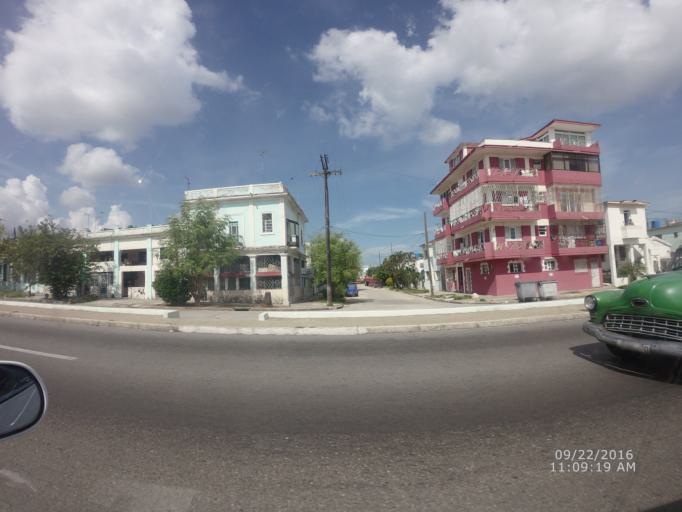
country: CU
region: La Habana
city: Cerro
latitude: 23.1081
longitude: -82.4189
